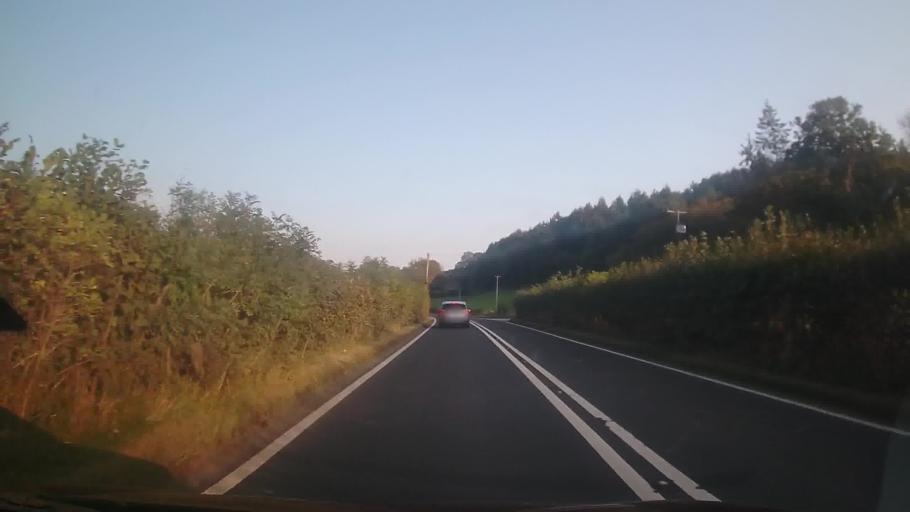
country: GB
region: Wales
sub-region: Sir Powys
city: Mochdre
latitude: 52.5037
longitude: -3.3639
